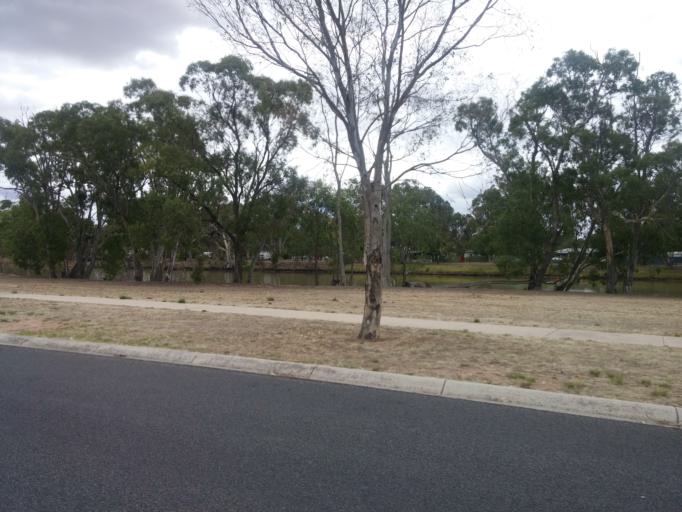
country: AU
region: Victoria
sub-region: Horsham
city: Horsham
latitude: -36.7244
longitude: 142.2004
